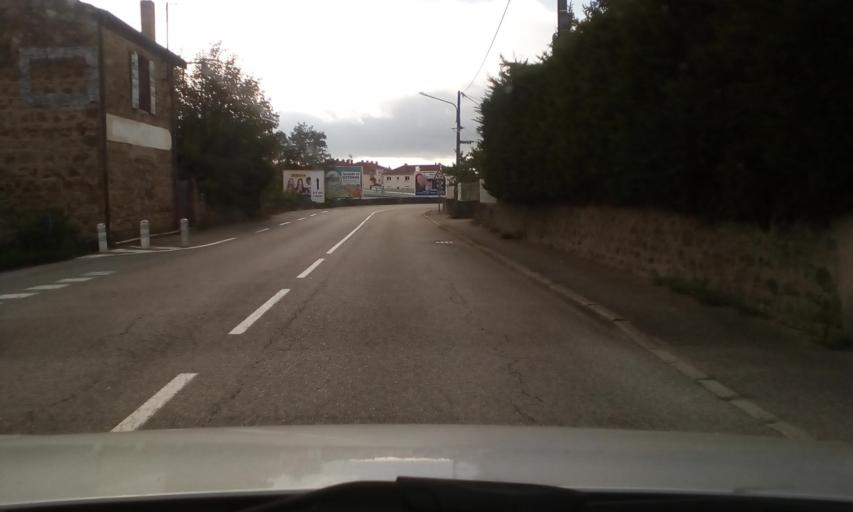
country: FR
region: Rhone-Alpes
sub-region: Departement de l'Ardeche
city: Boulieu-les-Annonay
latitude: 45.2578
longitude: 4.6675
